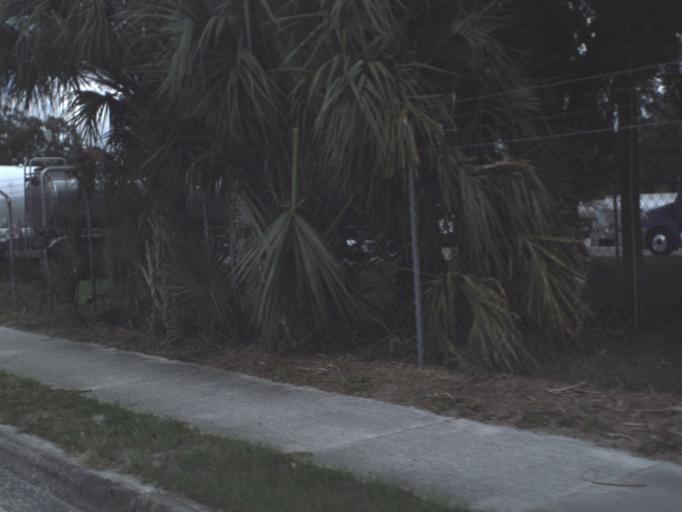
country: US
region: Florida
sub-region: Hillsborough County
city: East Lake-Orient Park
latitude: 27.9786
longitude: -82.4140
